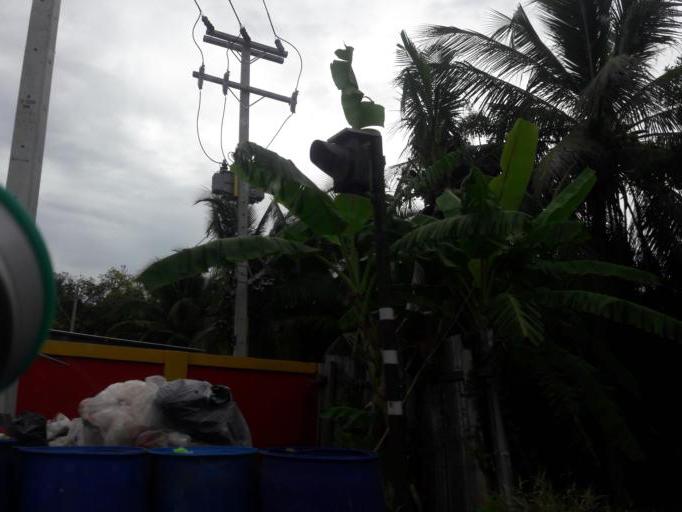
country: TH
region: Ratchaburi
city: Damnoen Saduak
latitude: 13.5393
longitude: 100.0112
